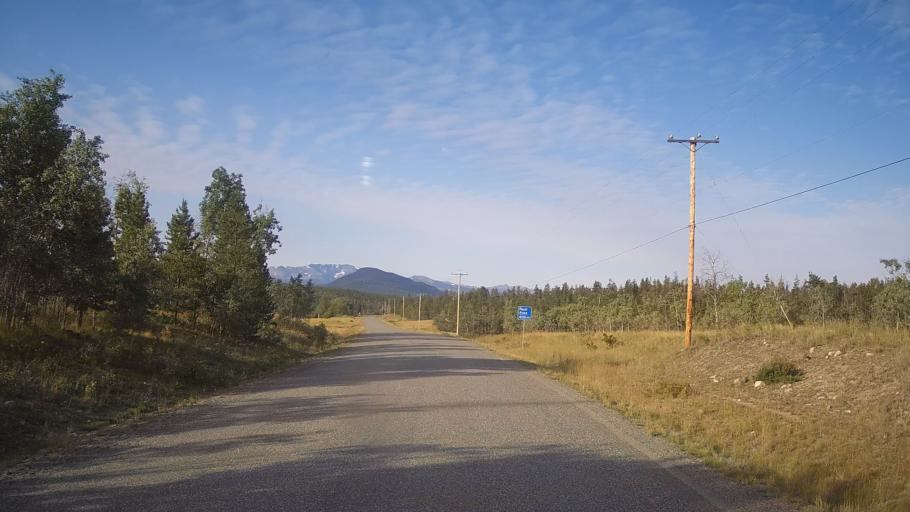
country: CA
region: British Columbia
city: Hanceville
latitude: 51.9458
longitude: -124.4582
